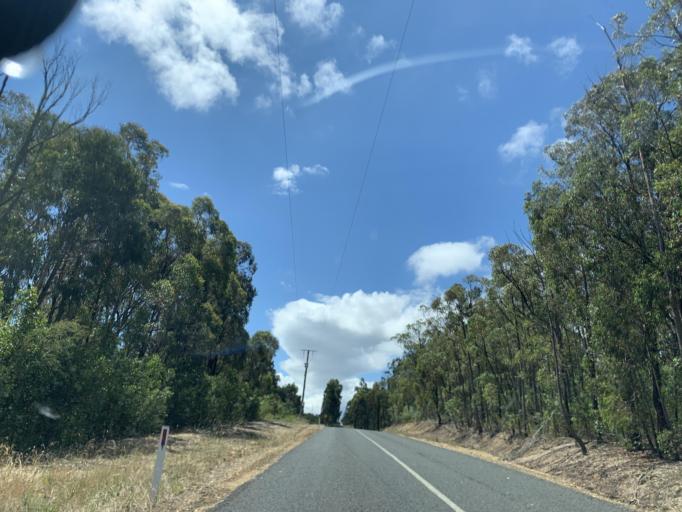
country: AU
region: Victoria
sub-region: Wellington
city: Heyfield
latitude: -37.9624
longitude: 146.6972
